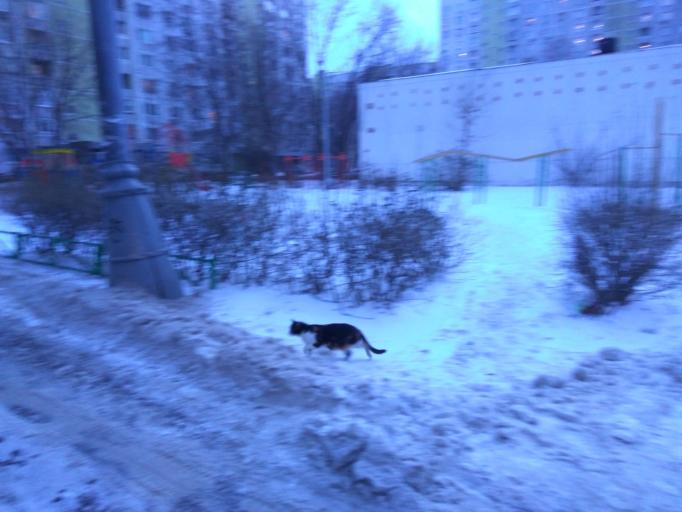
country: RU
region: Moscow
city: Mar'ino
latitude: 55.6506
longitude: 37.7098
